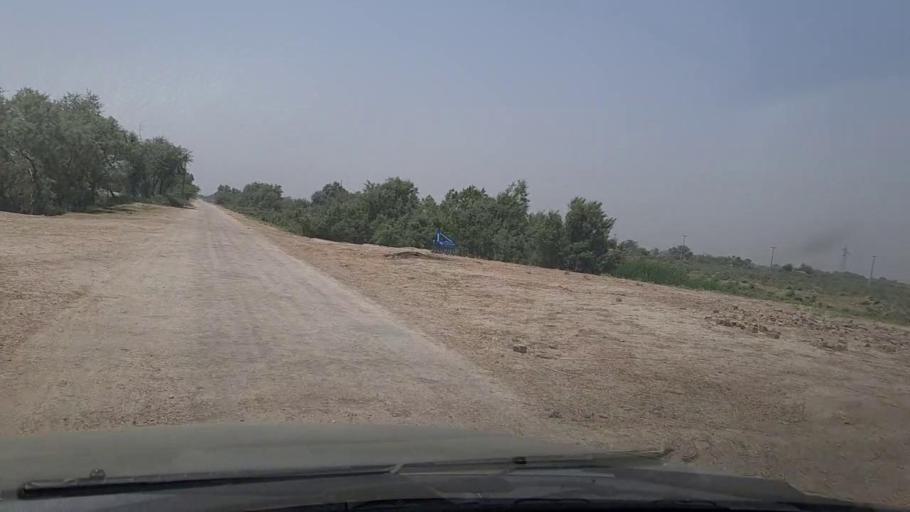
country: PK
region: Sindh
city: Ratodero
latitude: 27.7895
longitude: 68.2175
